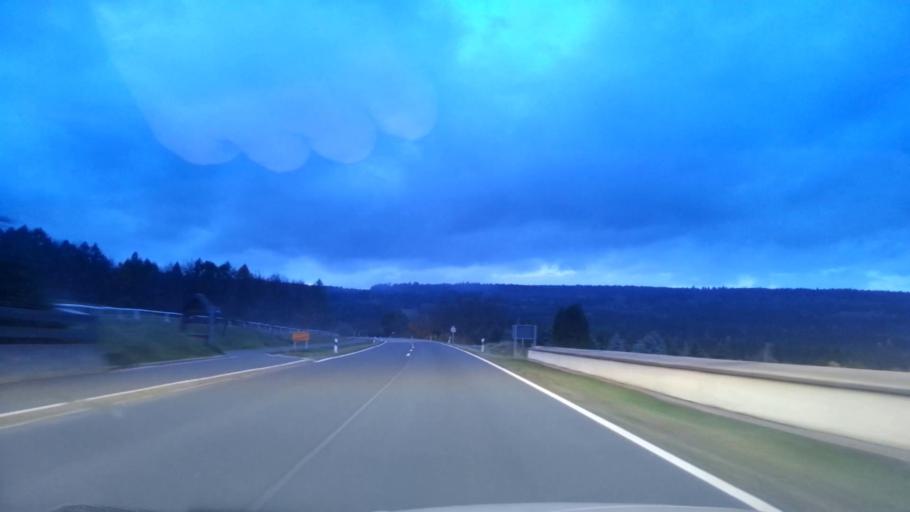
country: DE
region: Bavaria
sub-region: Upper Palatinate
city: Fuchsmuhl
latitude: 49.9276
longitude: 12.1420
